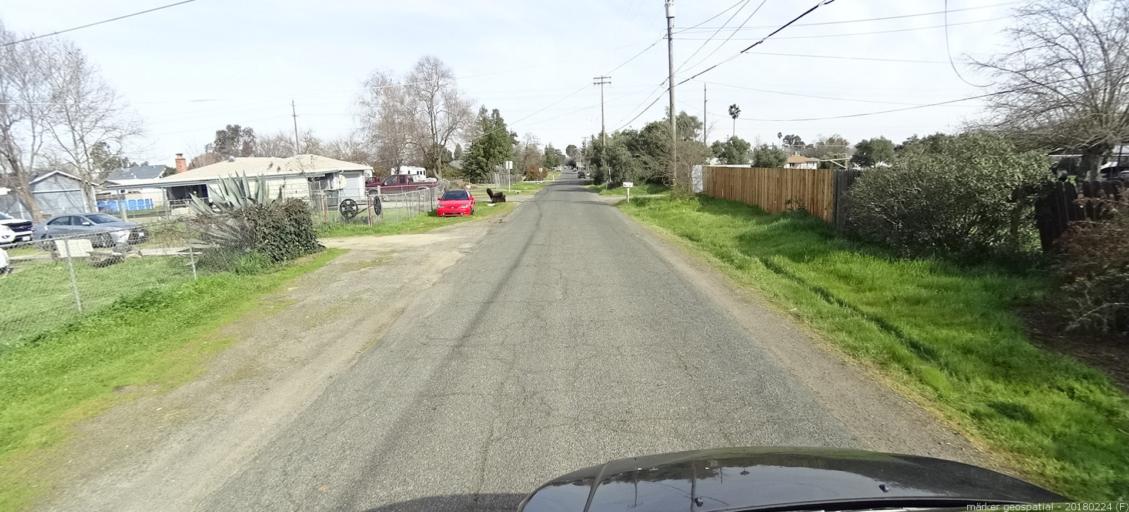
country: US
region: California
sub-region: Sacramento County
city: Rio Linda
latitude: 38.6975
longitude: -121.4615
